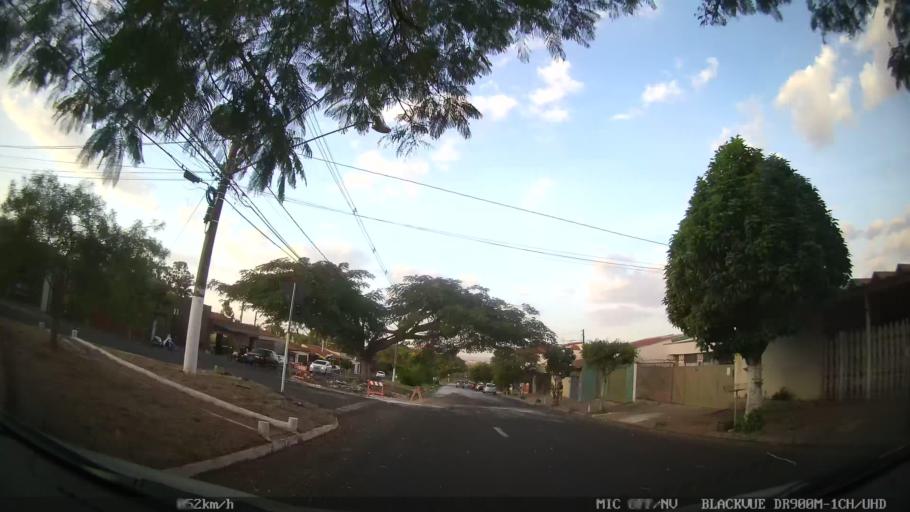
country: BR
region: Sao Paulo
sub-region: Ribeirao Preto
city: Ribeirao Preto
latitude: -21.1330
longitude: -47.8422
